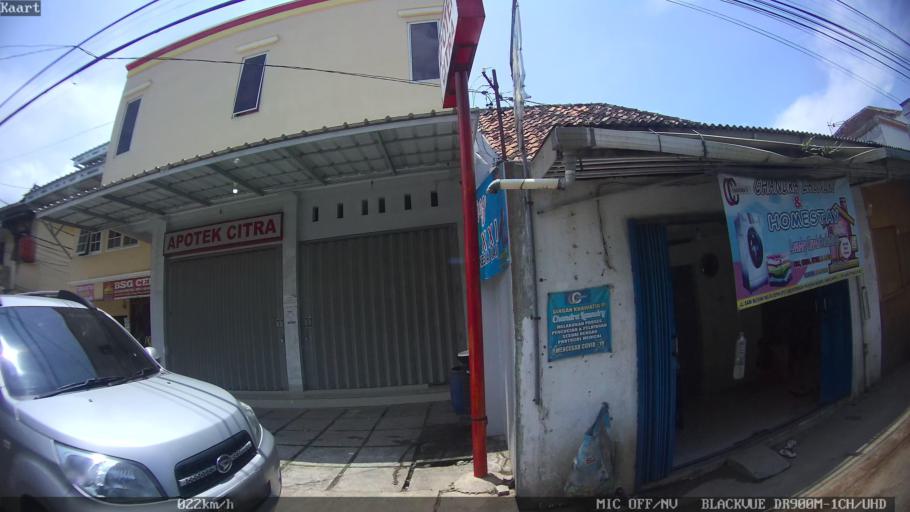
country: ID
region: Lampung
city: Kedaton
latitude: -5.4007
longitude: 105.2576
